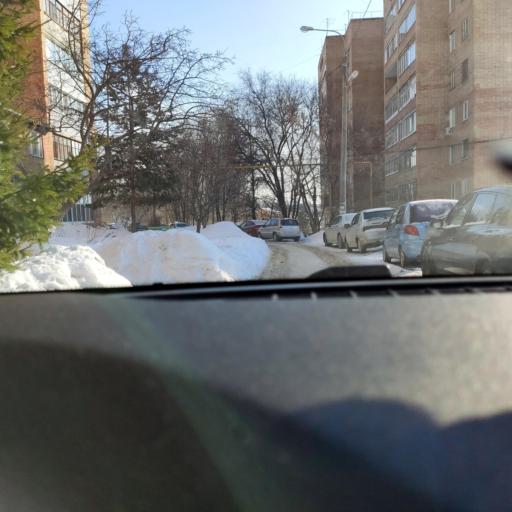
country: RU
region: Samara
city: Volzhskiy
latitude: 53.3429
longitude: 50.2153
